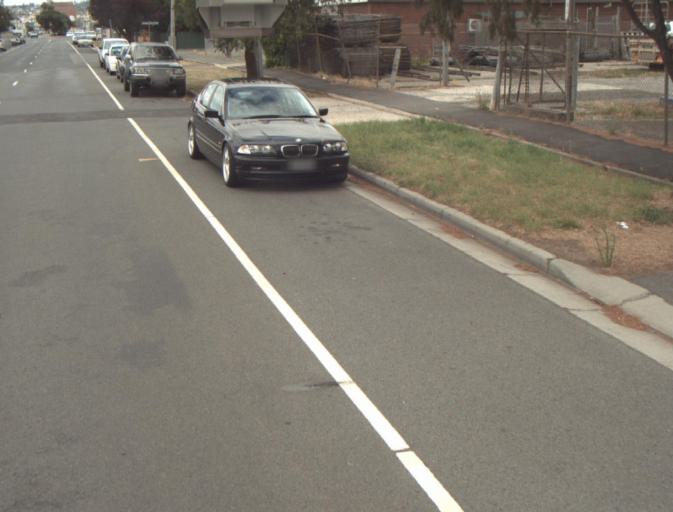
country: AU
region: Tasmania
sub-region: Launceston
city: Launceston
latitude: -41.4230
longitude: 147.1332
